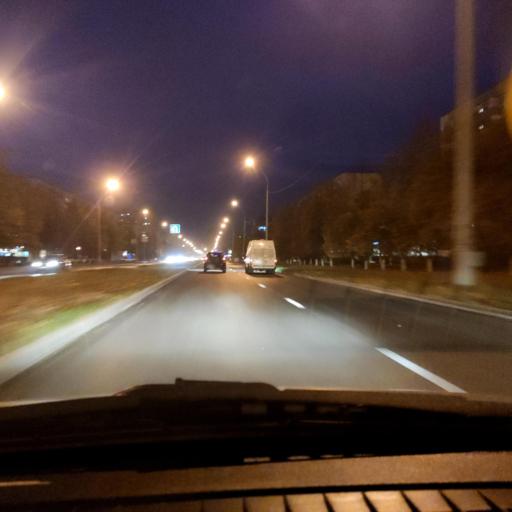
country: RU
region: Samara
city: Tol'yatti
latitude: 53.5366
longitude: 49.3294
